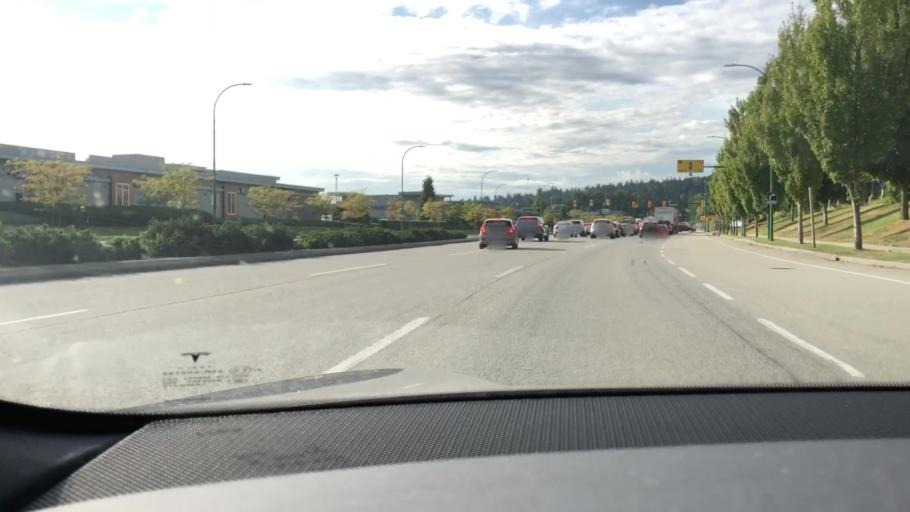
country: CA
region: British Columbia
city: New Westminster
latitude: 49.1985
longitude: -122.9770
